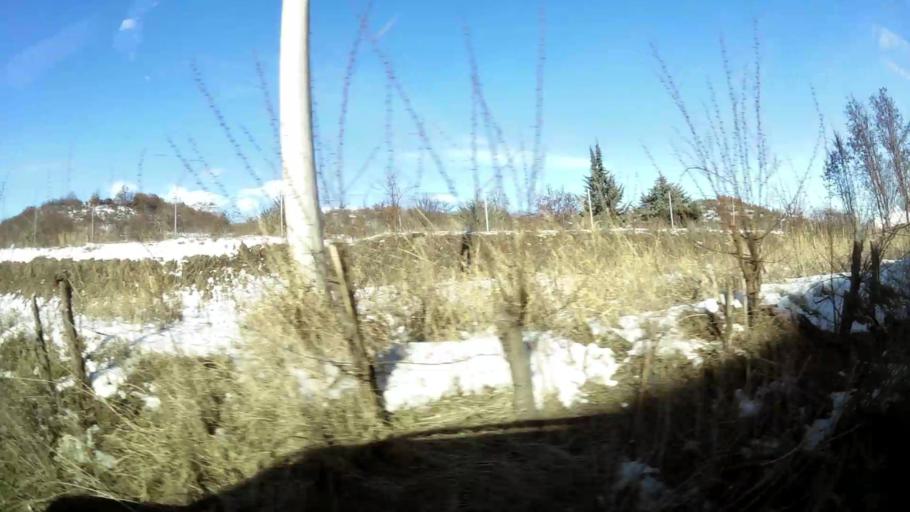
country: MK
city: Ljubin
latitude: 41.9876
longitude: 21.3087
